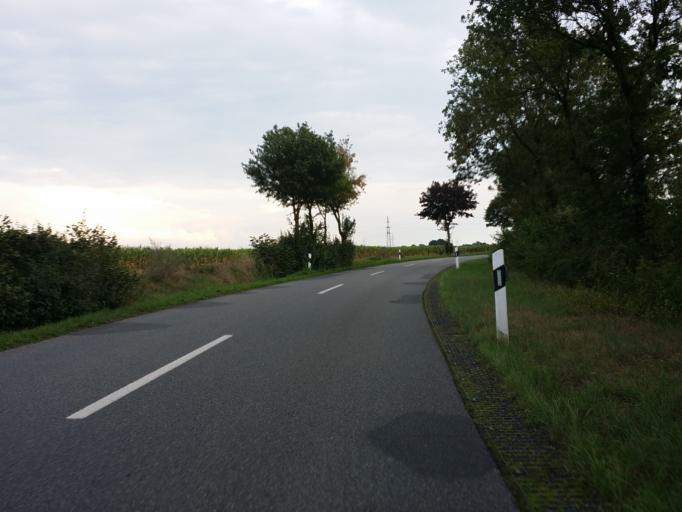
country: DE
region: Lower Saxony
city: Hollnseth
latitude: 53.5819
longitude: 9.1104
